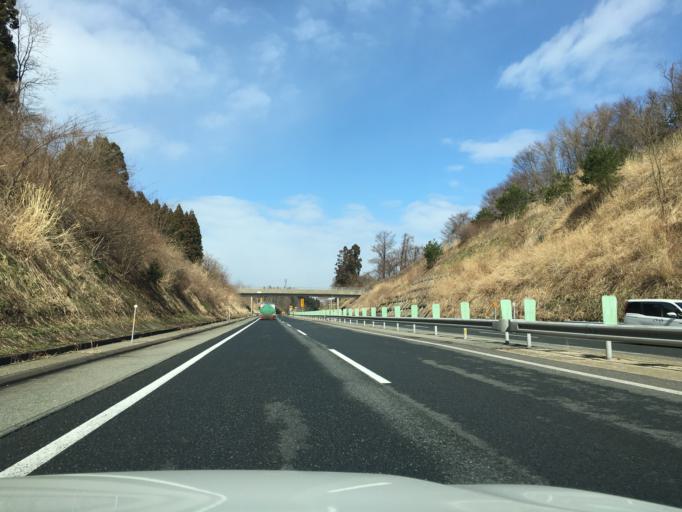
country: JP
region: Akita
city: Akita Shi
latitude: 39.7843
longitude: 140.1097
